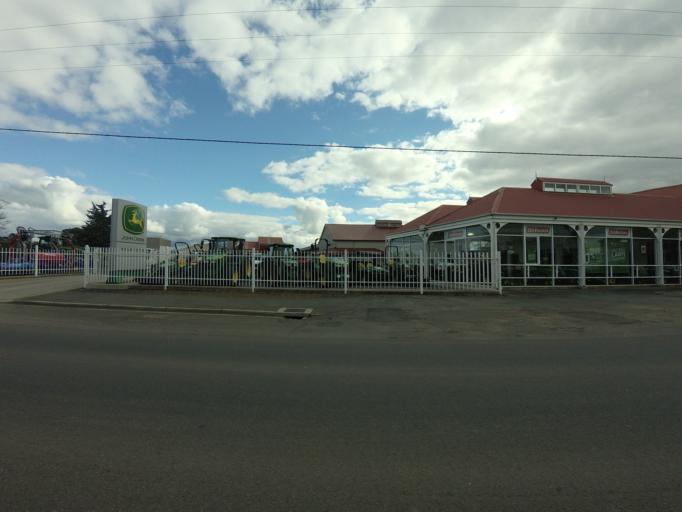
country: AU
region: Tasmania
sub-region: Northern Midlands
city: Longford
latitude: -41.5897
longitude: 147.1205
